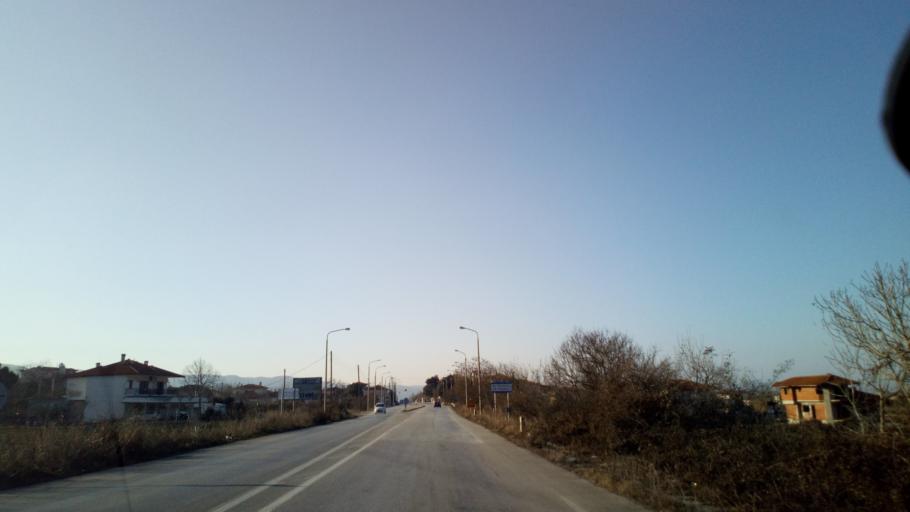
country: GR
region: Central Macedonia
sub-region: Nomos Thessalonikis
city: Agios Vasileios
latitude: 40.6625
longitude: 23.1194
